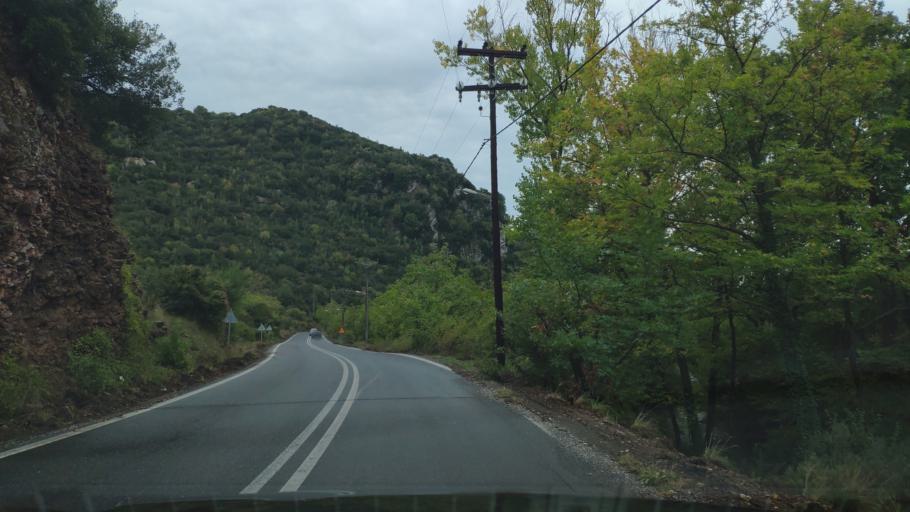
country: GR
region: Peloponnese
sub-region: Nomos Arkadias
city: Dimitsana
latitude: 37.6149
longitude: 22.0427
